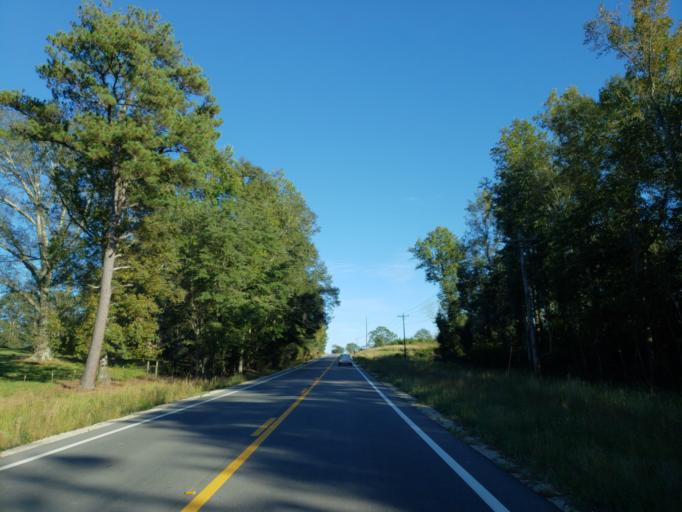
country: US
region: Mississippi
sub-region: Perry County
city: Richton
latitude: 31.3611
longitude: -89.0427
